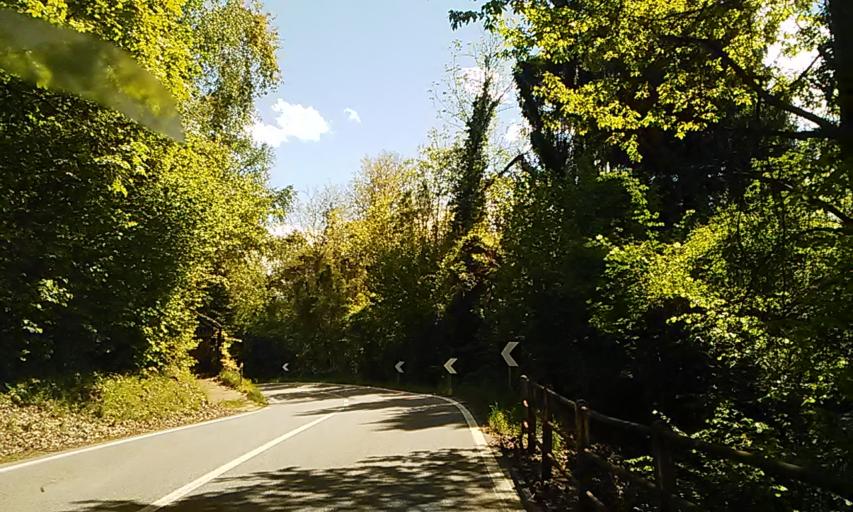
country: IT
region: Piedmont
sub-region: Provincia di Vercelli
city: Cellio
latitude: 45.7496
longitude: 8.3123
